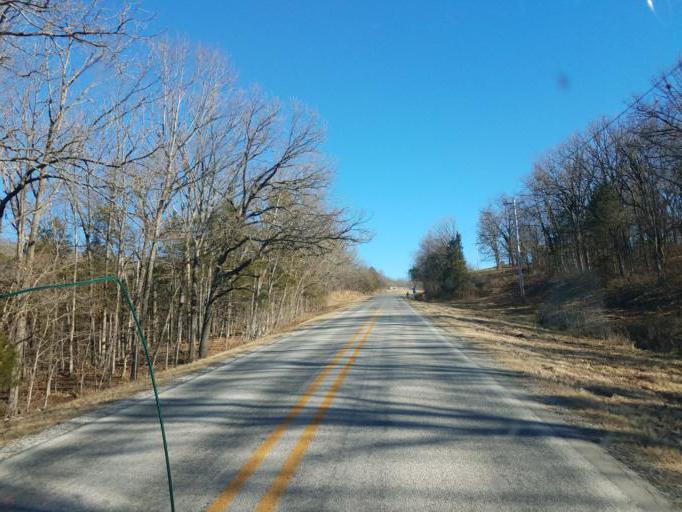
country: US
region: Arkansas
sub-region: Washington County
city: Elkins
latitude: 36.0265
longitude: -93.9975
